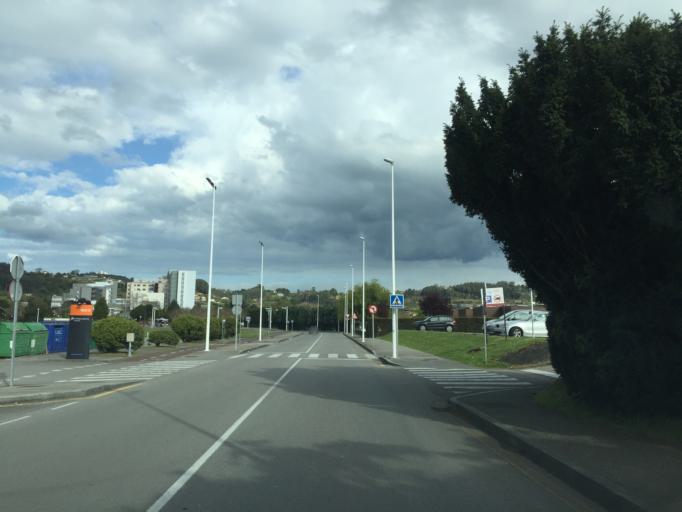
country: ES
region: Asturias
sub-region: Province of Asturias
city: Gijon
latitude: 43.5241
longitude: -5.6129
